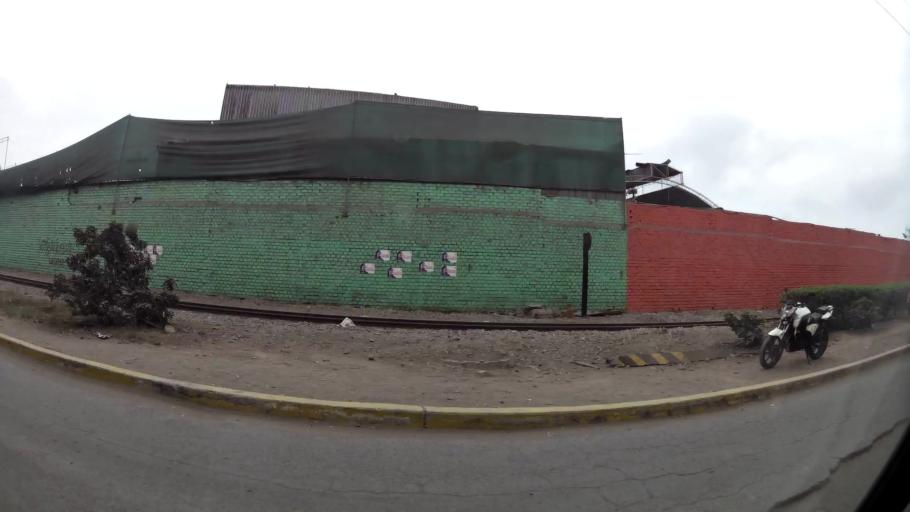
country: PE
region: Callao
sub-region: Callao
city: Callao
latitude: -12.0468
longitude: -77.1100
